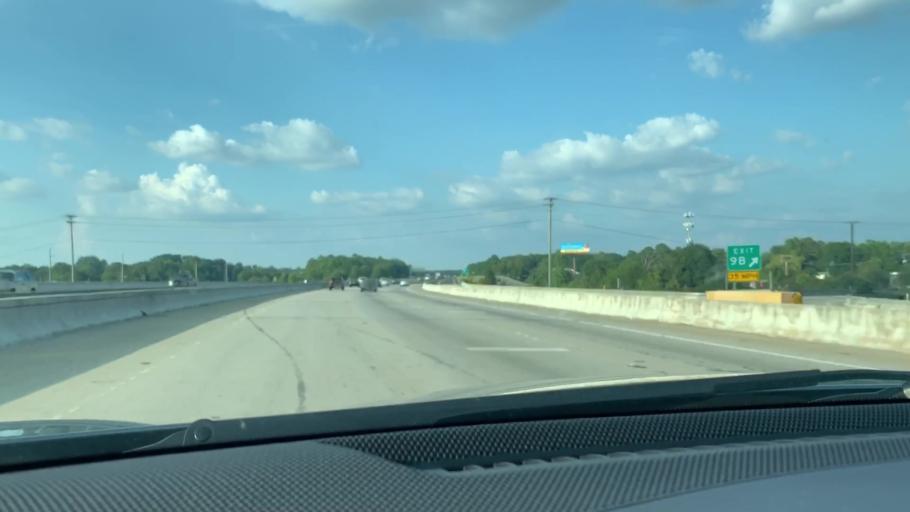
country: US
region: South Carolina
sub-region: Richland County
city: Forest Acres
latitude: 33.9744
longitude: -80.9550
